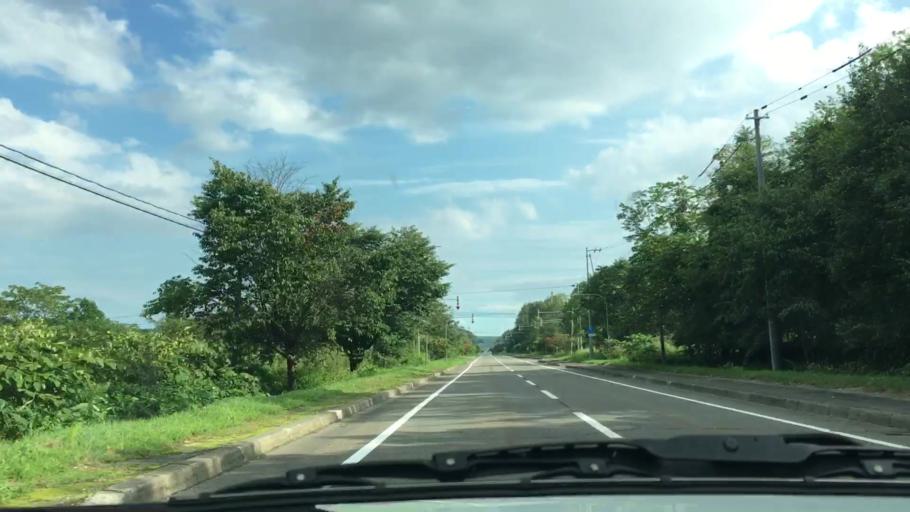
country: JP
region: Hokkaido
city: Otofuke
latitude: 43.3235
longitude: 143.3004
